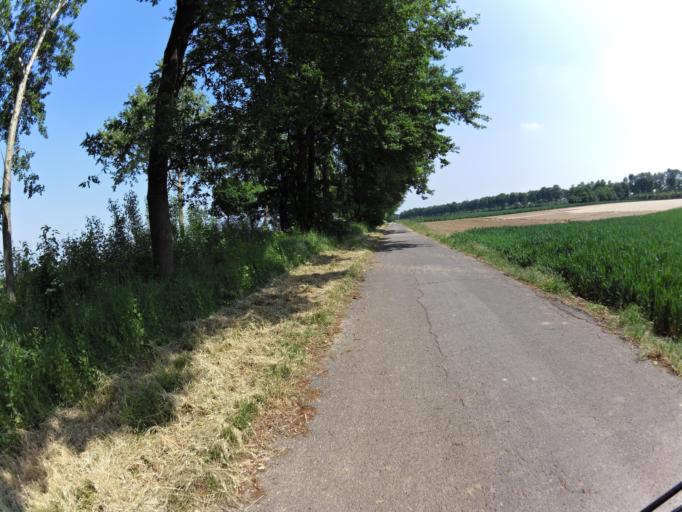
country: DE
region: North Rhine-Westphalia
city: Niedermerz
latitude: 50.8873
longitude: 6.2573
